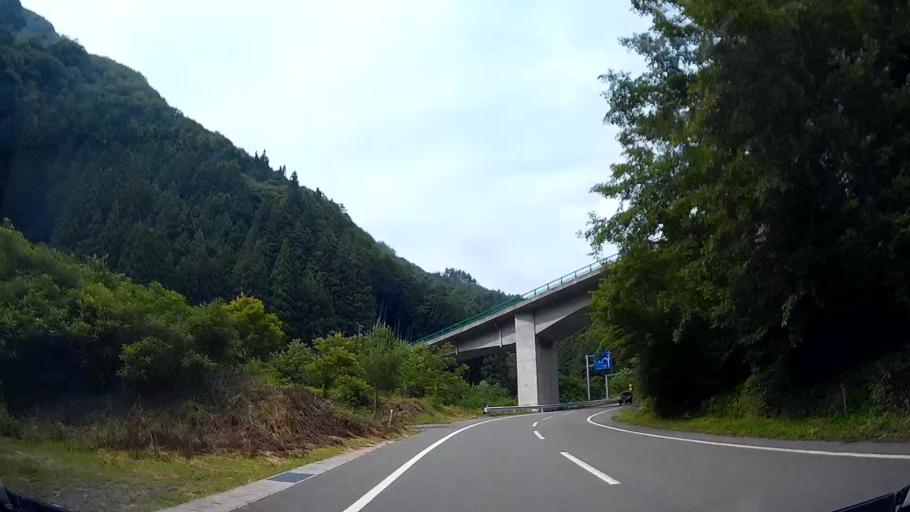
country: JP
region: Nagano
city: Iida
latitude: 35.4423
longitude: 137.9910
